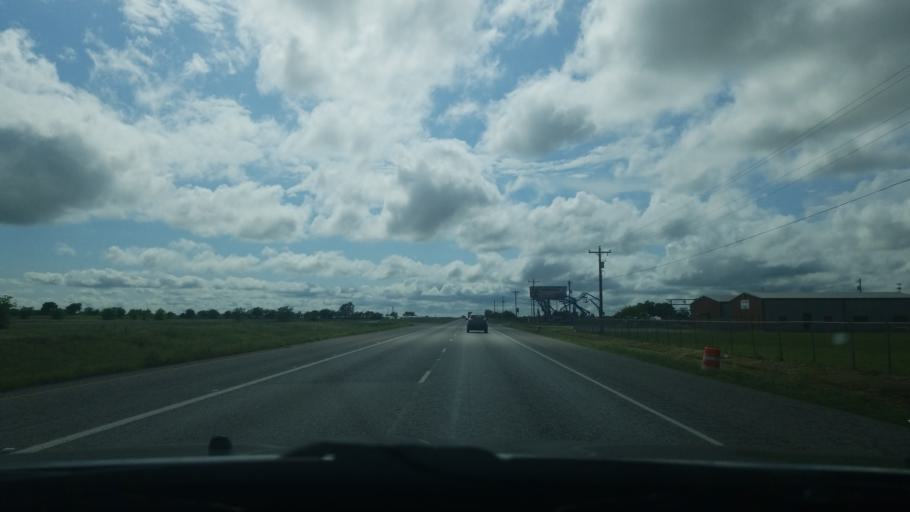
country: US
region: Texas
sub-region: Denton County
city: Ponder
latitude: 33.2389
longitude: -97.3267
